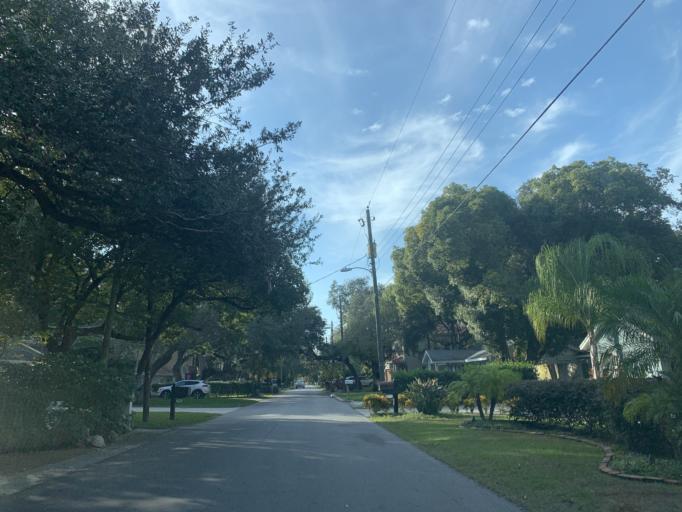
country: US
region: Florida
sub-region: Hillsborough County
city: Tampa
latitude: 27.8955
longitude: -82.4987
